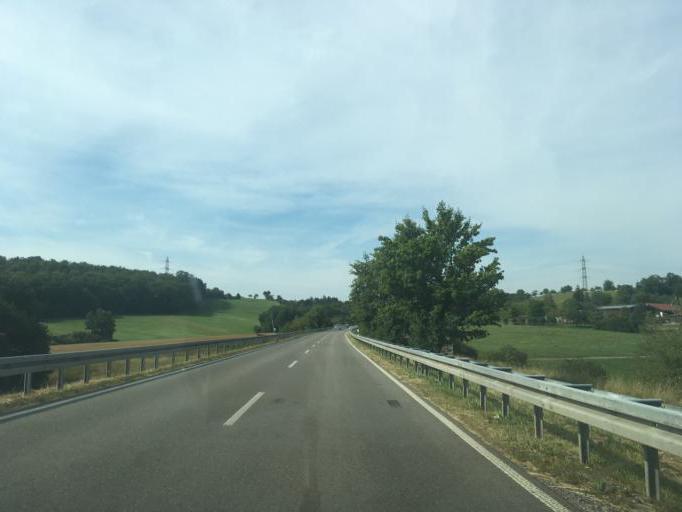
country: DE
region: Baden-Wuerttemberg
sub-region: Tuebingen Region
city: Dettenhausen
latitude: 48.6281
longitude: 9.0996
